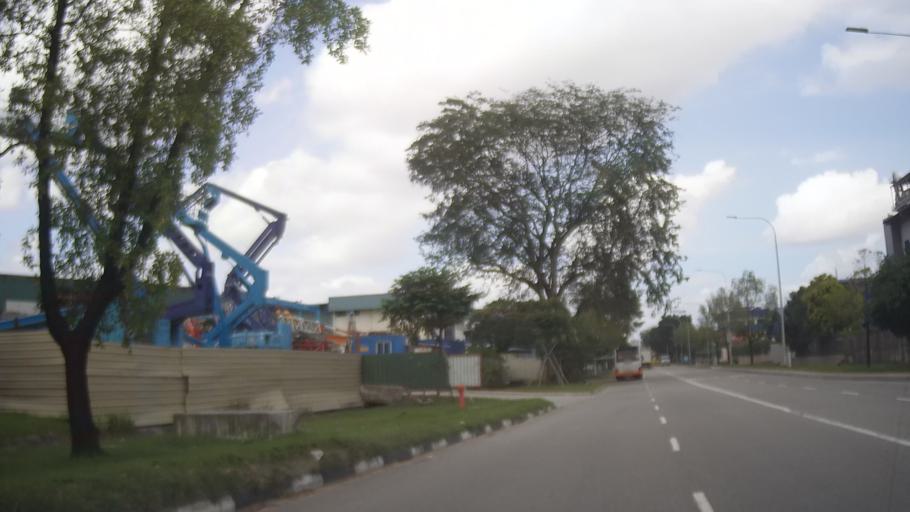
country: MY
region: Johor
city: Johor Bahru
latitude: 1.4309
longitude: 103.7470
